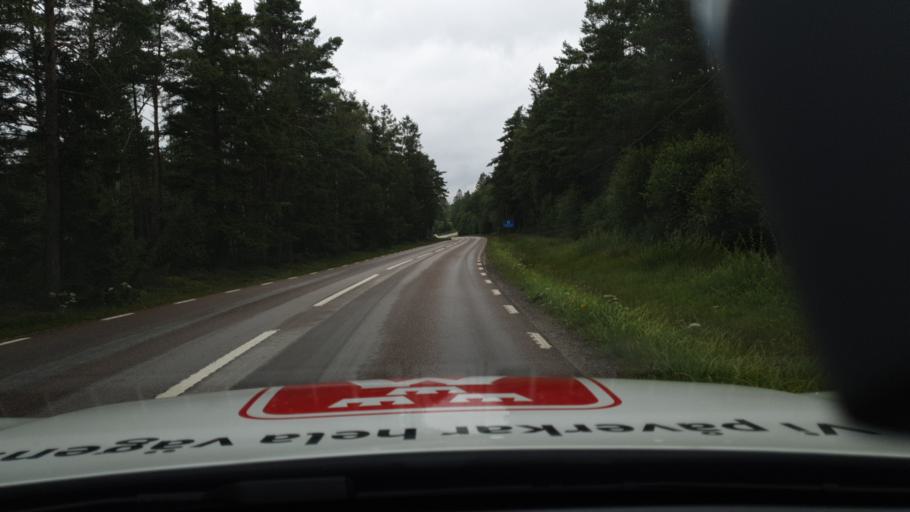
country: SE
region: Vaestra Goetaland
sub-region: Uddevalla Kommun
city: Ljungskile
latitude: 58.1765
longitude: 11.9947
